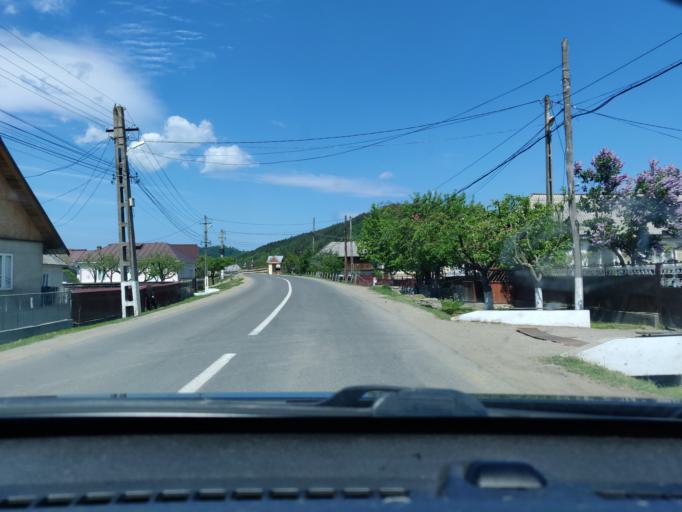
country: RO
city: Campurile de Jos
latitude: 46.0326
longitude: 26.7553
